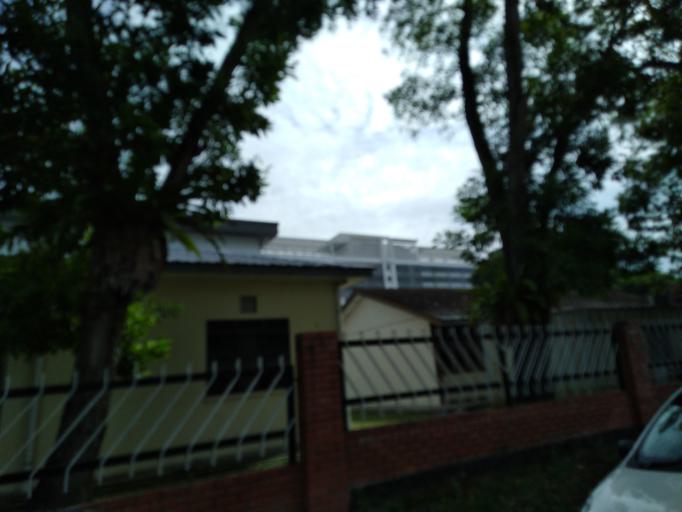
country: MY
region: Perak
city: Ipoh
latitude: 4.6016
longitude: 101.0877
